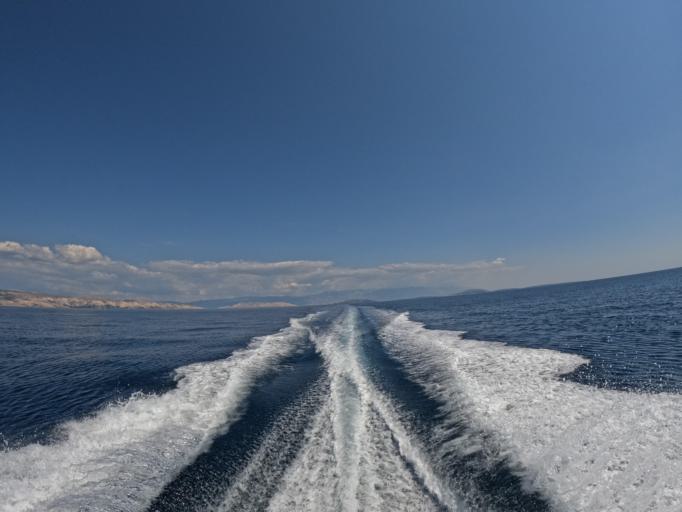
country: HR
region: Primorsko-Goranska
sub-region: Grad Krk
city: Krk
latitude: 44.9207
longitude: 14.5631
